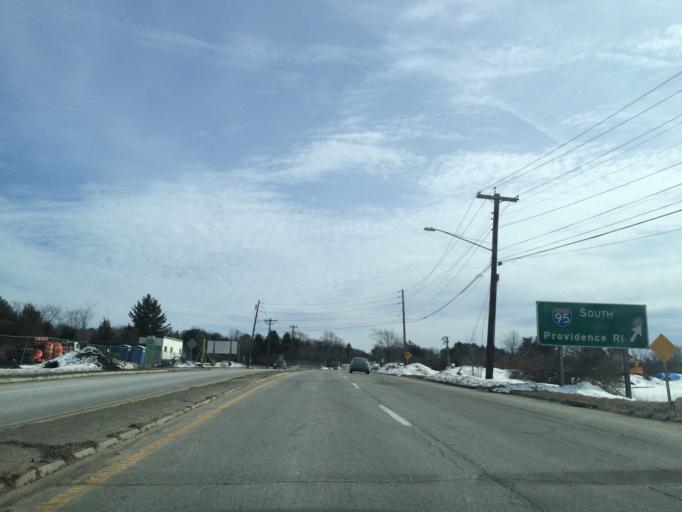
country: US
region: Massachusetts
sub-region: Middlesex County
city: Lexington
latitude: 42.4720
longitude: -71.2464
